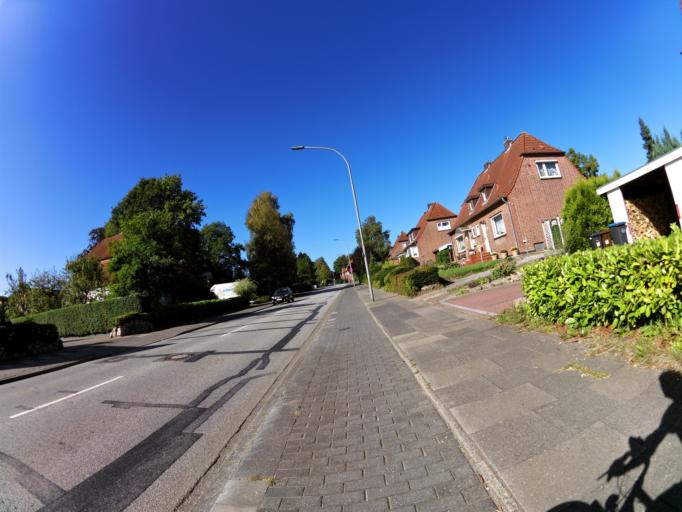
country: DE
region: Schleswig-Holstein
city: Eckernforde
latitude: 54.4534
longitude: 9.8482
